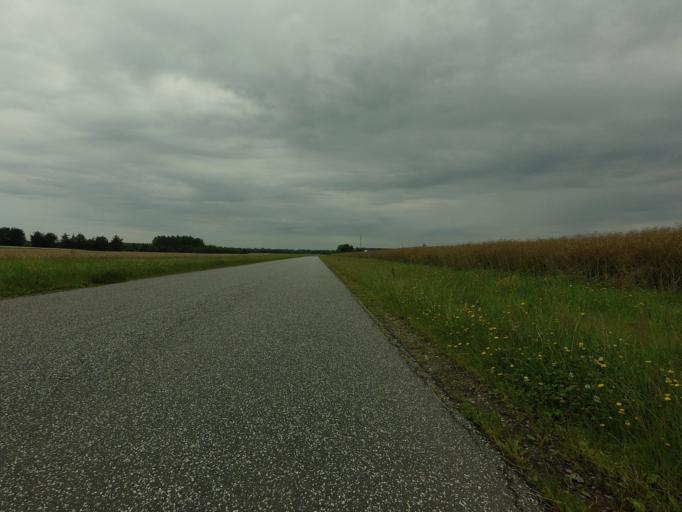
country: DK
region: North Denmark
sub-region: Alborg Kommune
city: Vadum
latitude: 57.1277
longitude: 9.8540
